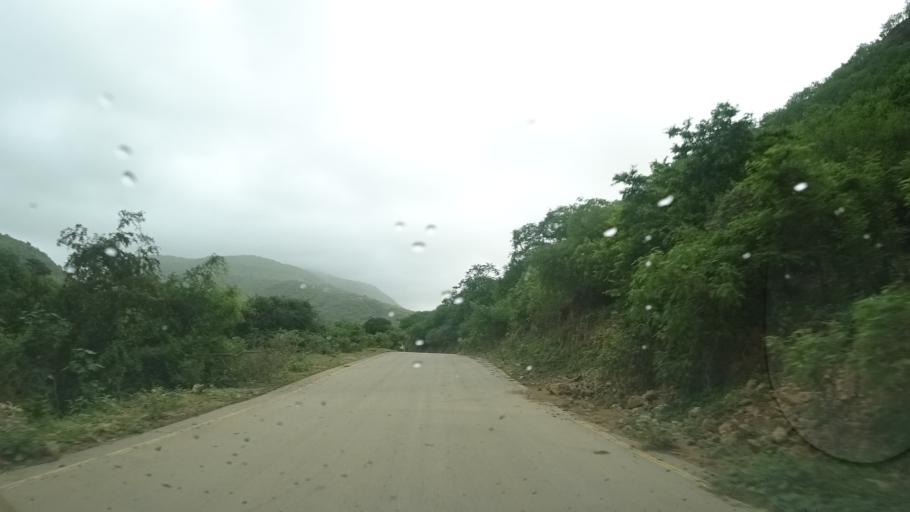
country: OM
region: Zufar
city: Salalah
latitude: 17.0963
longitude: 54.3291
